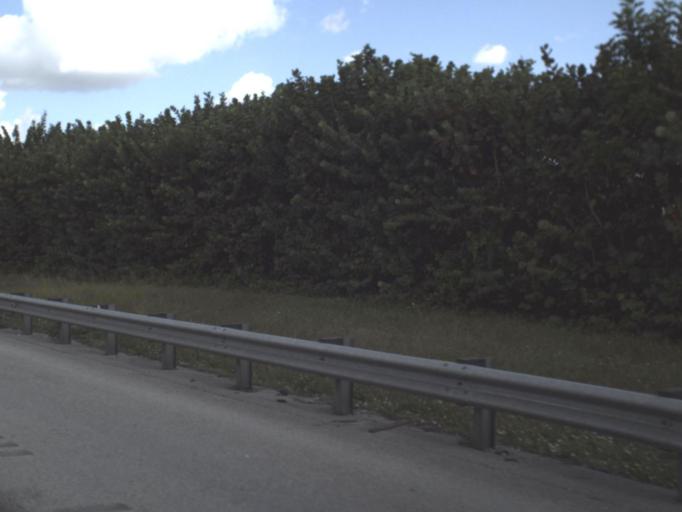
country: US
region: Florida
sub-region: Palm Beach County
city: Boca Pointe
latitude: 26.3420
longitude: -80.1703
